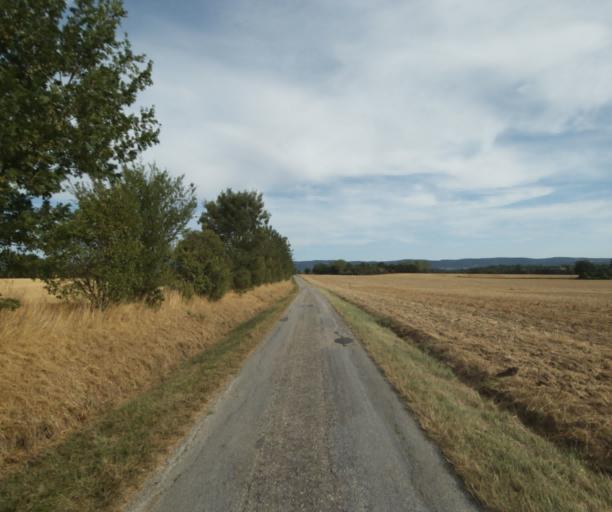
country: FR
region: Midi-Pyrenees
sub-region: Departement du Tarn
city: Puylaurens
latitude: 43.5276
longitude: 2.0380
